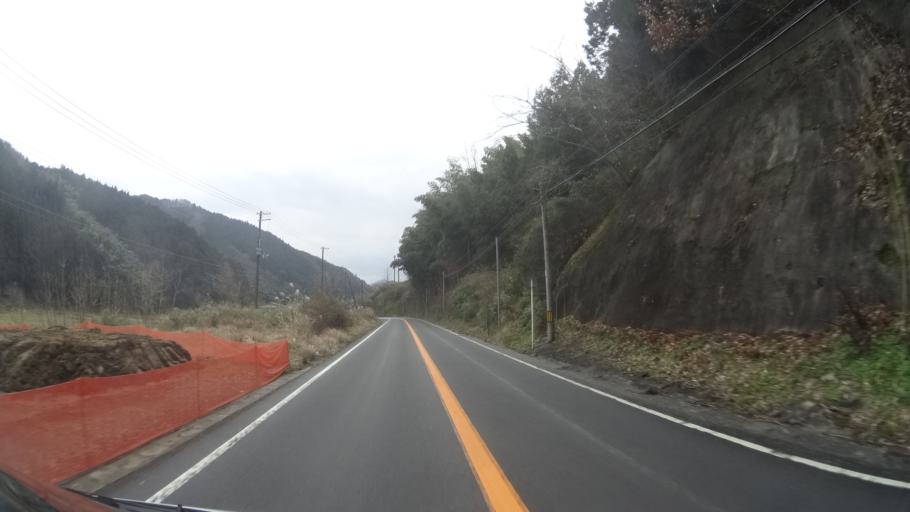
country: JP
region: Kyoto
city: Fukuchiyama
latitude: 35.3691
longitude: 135.0482
